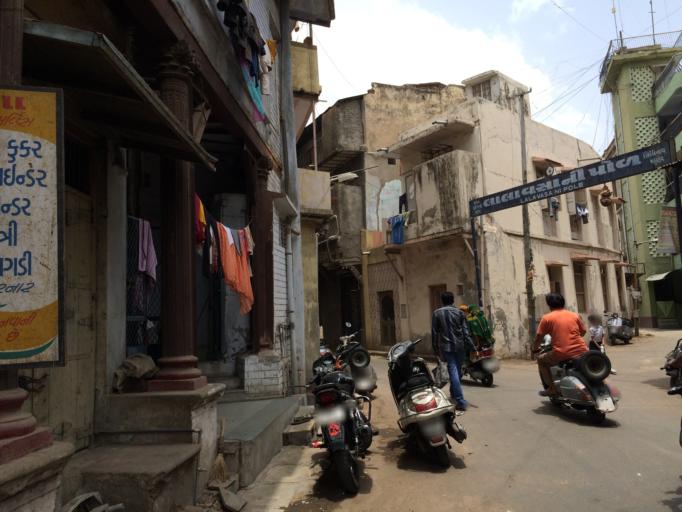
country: IN
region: Gujarat
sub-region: Ahmadabad
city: Ahmedabad
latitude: 23.0218
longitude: 72.5929
